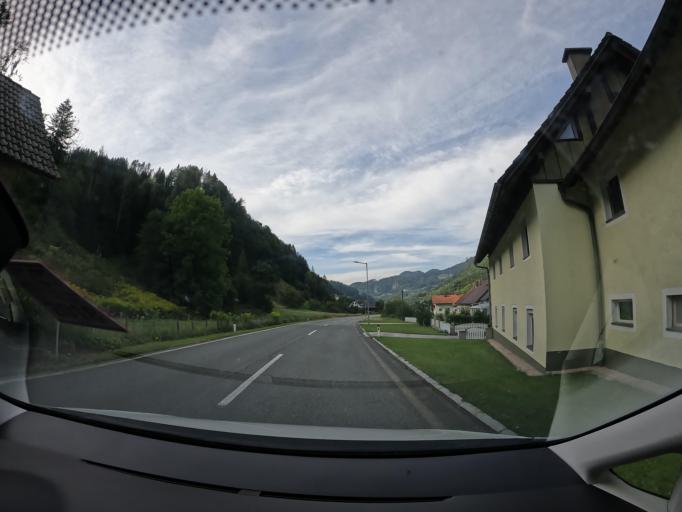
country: AT
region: Carinthia
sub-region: Politischer Bezirk Volkermarkt
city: Bad Eisenkappel
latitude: 46.4678
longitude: 14.5926
